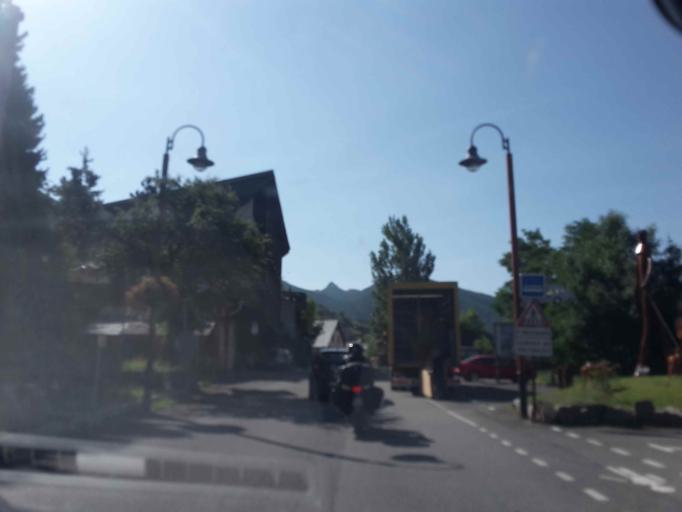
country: FR
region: Provence-Alpes-Cote d'Azur
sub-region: Departement des Hautes-Alpes
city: Guillestre
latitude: 44.6115
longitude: 6.6874
